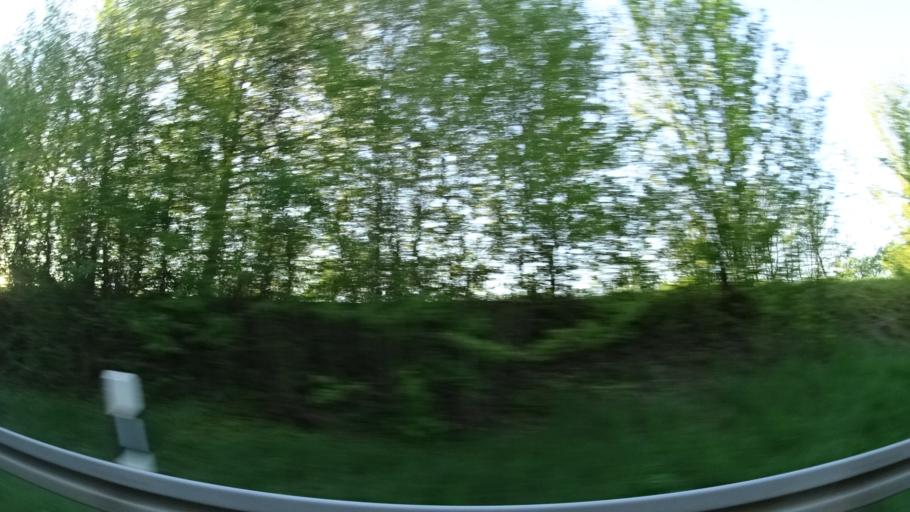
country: DE
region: Baden-Wuerttemberg
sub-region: Regierungsbezirk Stuttgart
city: Neuenstein
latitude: 49.2056
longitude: 9.5927
